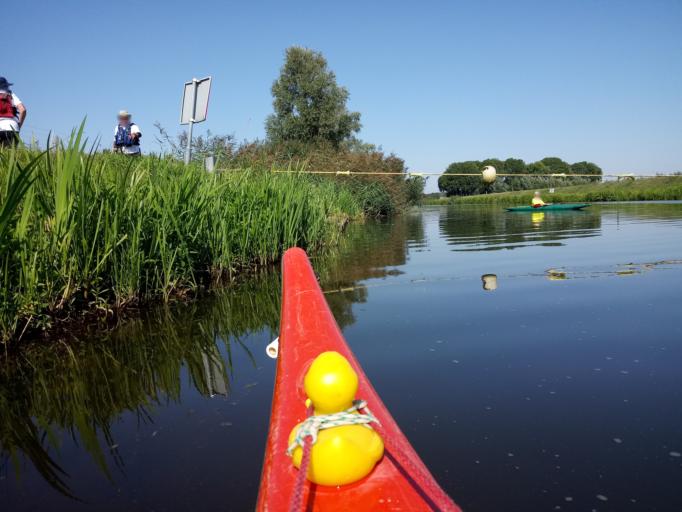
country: NL
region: Gelderland
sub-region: Berkelland
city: Eibergen
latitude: 52.1001
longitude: 6.7034
